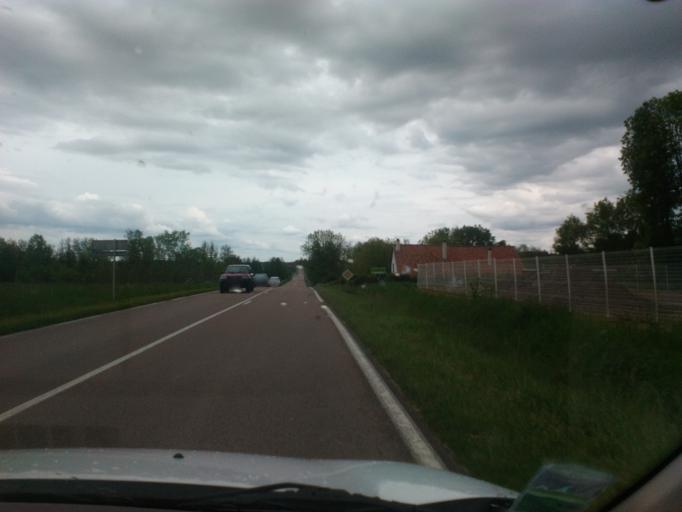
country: FR
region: Champagne-Ardenne
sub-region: Departement de l'Aube
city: Lusigny-sur-Barse
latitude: 48.2438
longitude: 4.2825
